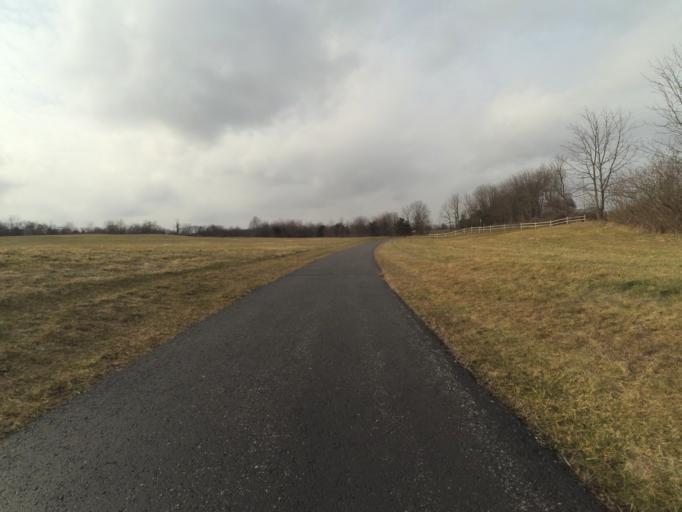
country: US
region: Pennsylvania
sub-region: Centre County
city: Park Forest Village
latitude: 40.7990
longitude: -77.8907
